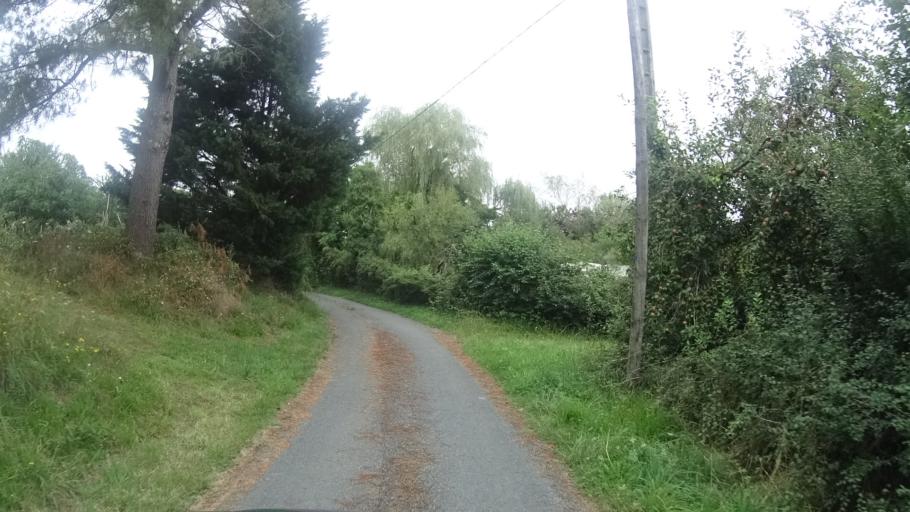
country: FR
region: Aquitaine
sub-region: Departement de la Dordogne
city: Sourzac
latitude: 44.9795
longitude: 0.4713
